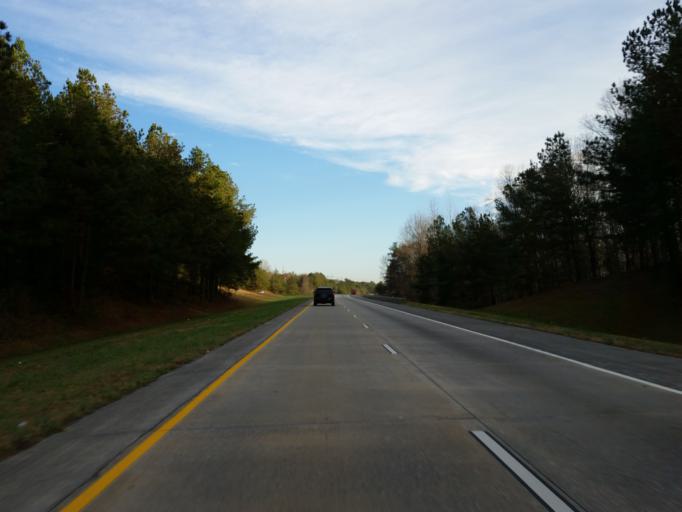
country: US
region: Georgia
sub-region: Cherokee County
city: Canton
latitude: 34.2843
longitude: -84.4468
